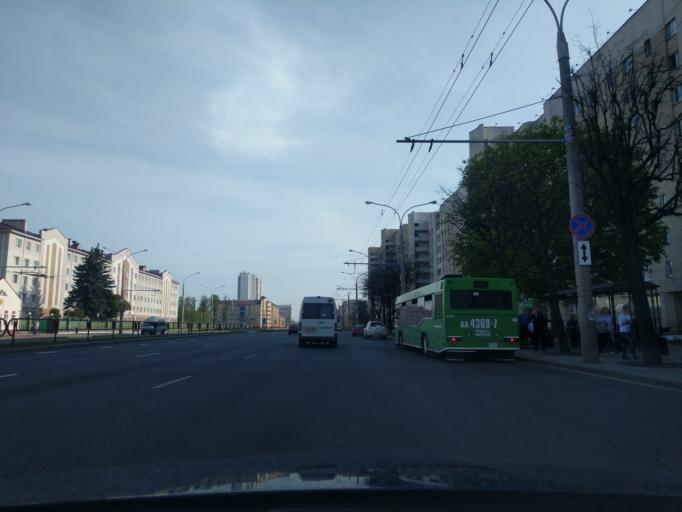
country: BY
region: Minsk
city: Minsk
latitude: 53.8689
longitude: 27.5699
